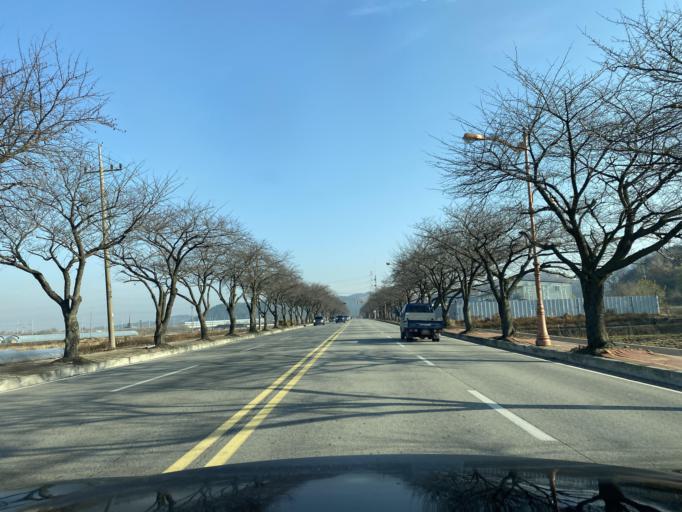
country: KR
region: Chungcheongnam-do
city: Yesan
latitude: 36.7292
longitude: 126.8563
